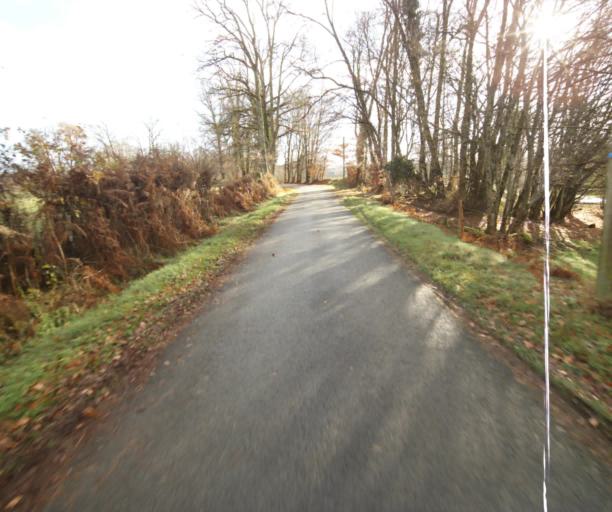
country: FR
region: Limousin
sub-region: Departement de la Correze
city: Sainte-Fereole
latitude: 45.2546
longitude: 1.6079
